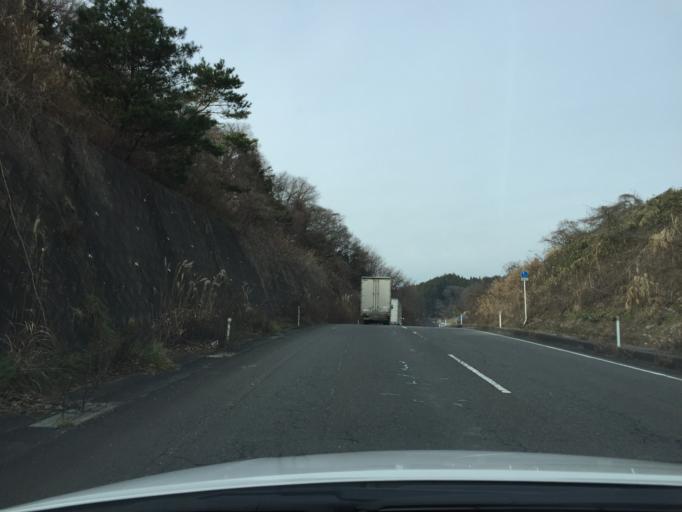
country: JP
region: Fukushima
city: Funehikimachi-funehiki
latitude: 37.2819
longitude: 140.6206
